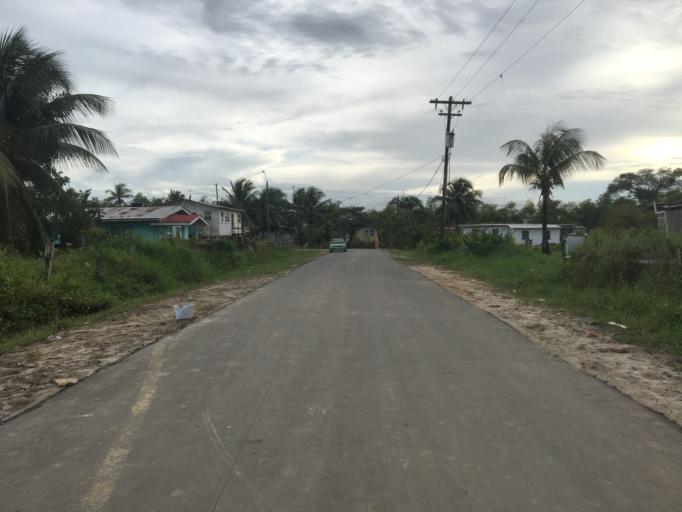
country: GY
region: Demerara-Mahaica
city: Georgetown
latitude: 6.7912
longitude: -58.1235
